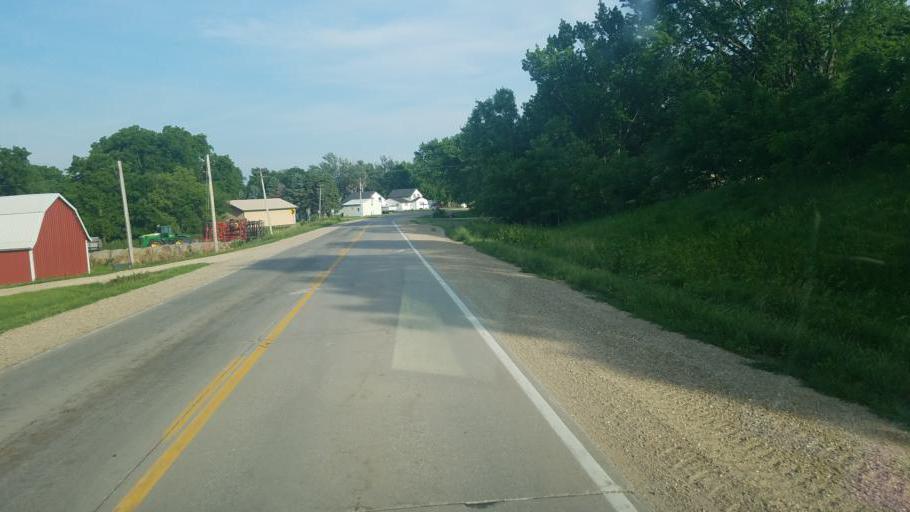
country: US
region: Iowa
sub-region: Tama County
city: Toledo
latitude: 41.9840
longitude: -92.7162
